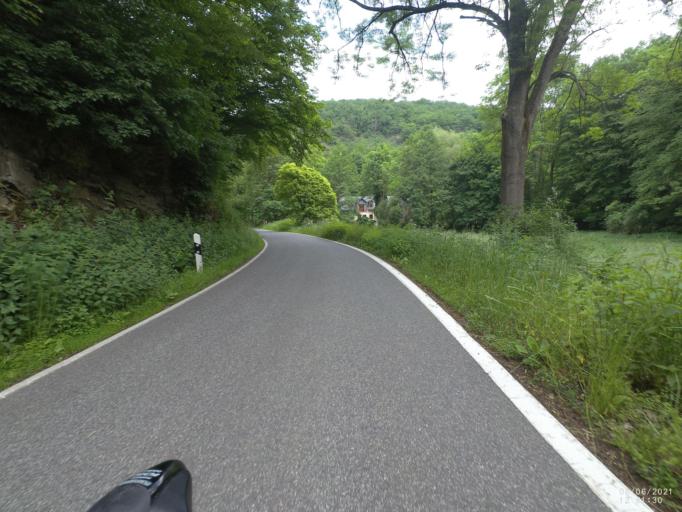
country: DE
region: Rheinland-Pfalz
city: Hatzenport
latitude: 50.2366
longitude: 7.4031
